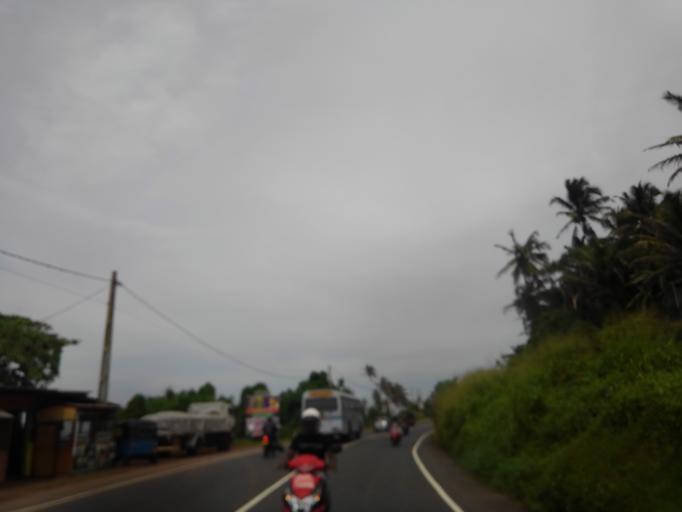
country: LK
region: Western
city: Beruwala
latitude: 6.4887
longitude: 79.9828
